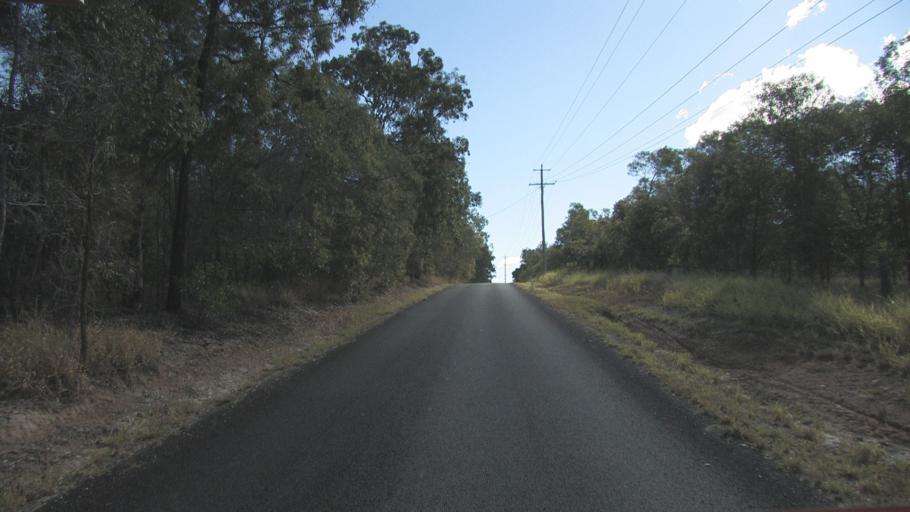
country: AU
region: Queensland
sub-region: Ipswich
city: Springfield Lakes
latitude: -27.7357
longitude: 152.9351
